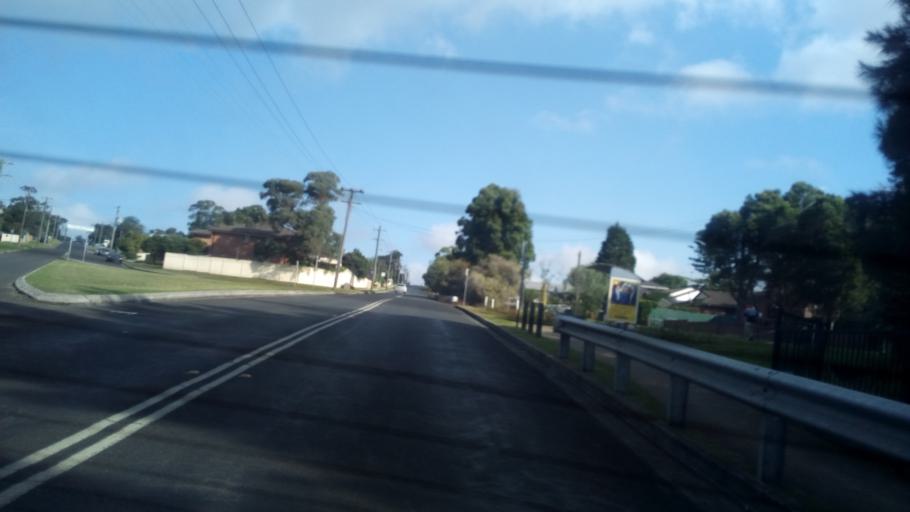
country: AU
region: New South Wales
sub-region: Wollongong
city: Helensburgh
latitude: -34.1954
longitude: 150.9812
